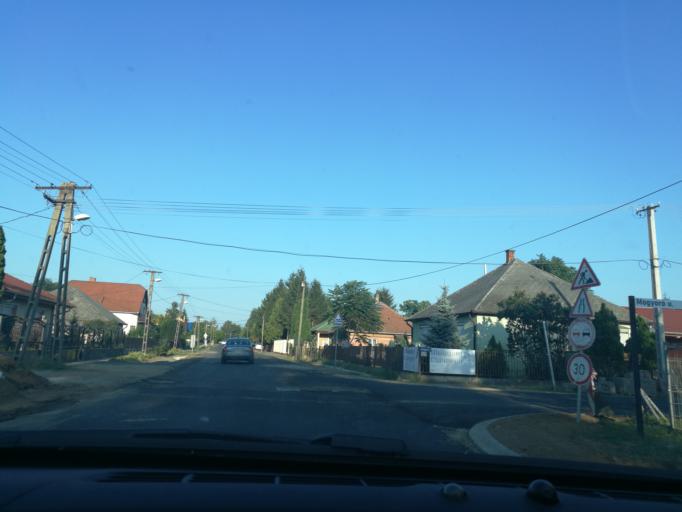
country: HU
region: Szabolcs-Szatmar-Bereg
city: Kotaj
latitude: 48.0044
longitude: 21.7373
